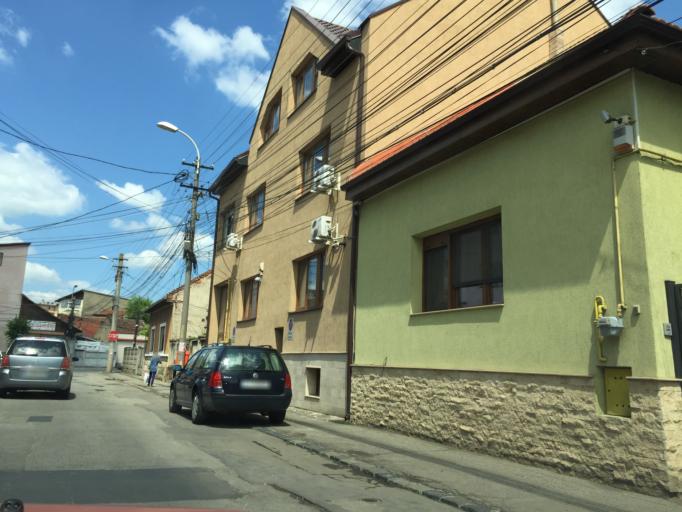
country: RO
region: Cluj
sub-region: Municipiul Cluj-Napoca
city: Cluj-Napoca
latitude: 46.7815
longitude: 23.5911
